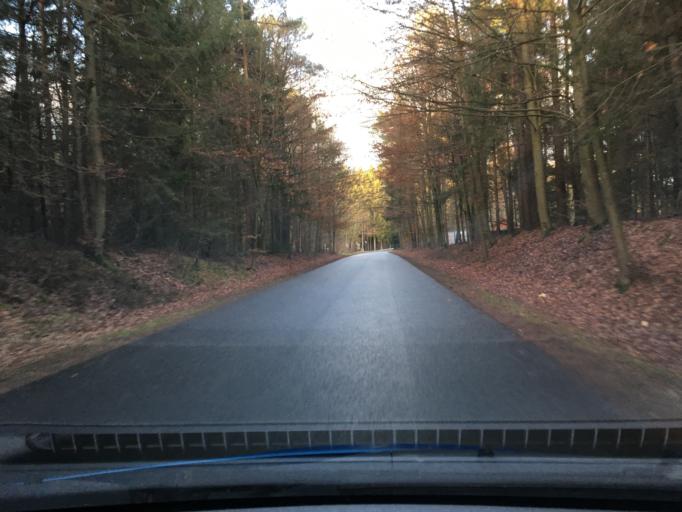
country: DE
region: Lower Saxony
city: Soderstorf
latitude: 53.0980
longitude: 10.1540
